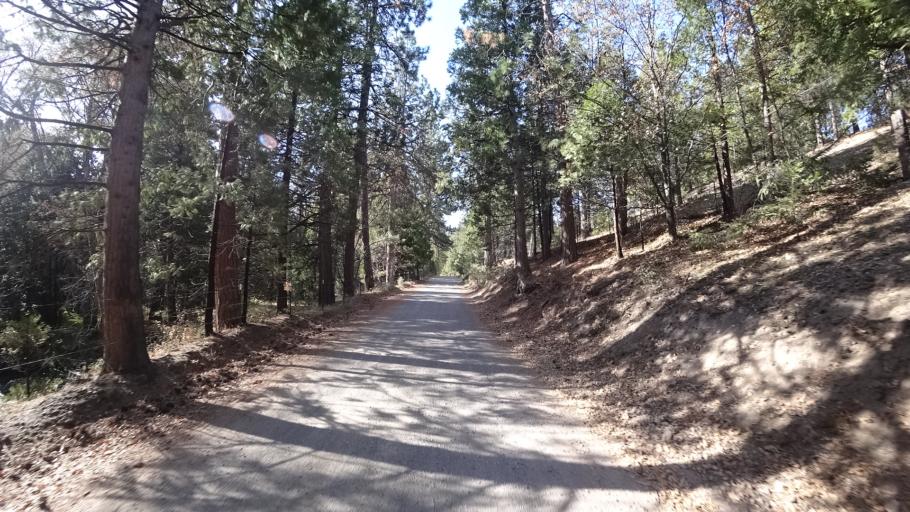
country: US
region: California
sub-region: Siskiyou County
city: Weed
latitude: 41.4342
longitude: -122.4179
